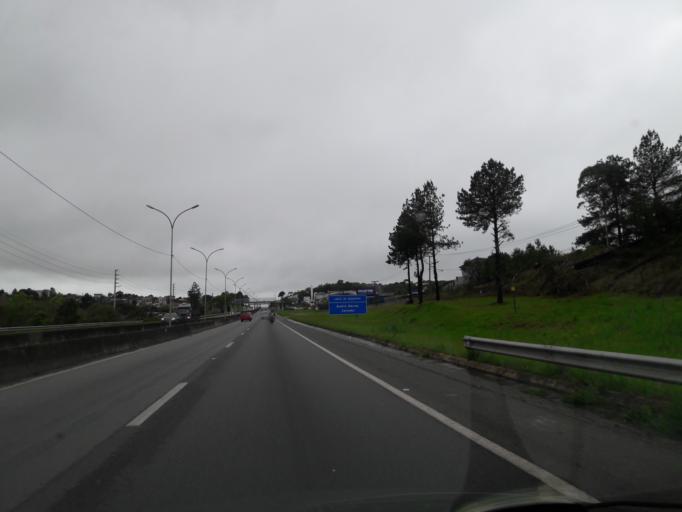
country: BR
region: Parana
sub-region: Quatro Barras
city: Quatro Barras
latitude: -25.3705
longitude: -49.1231
